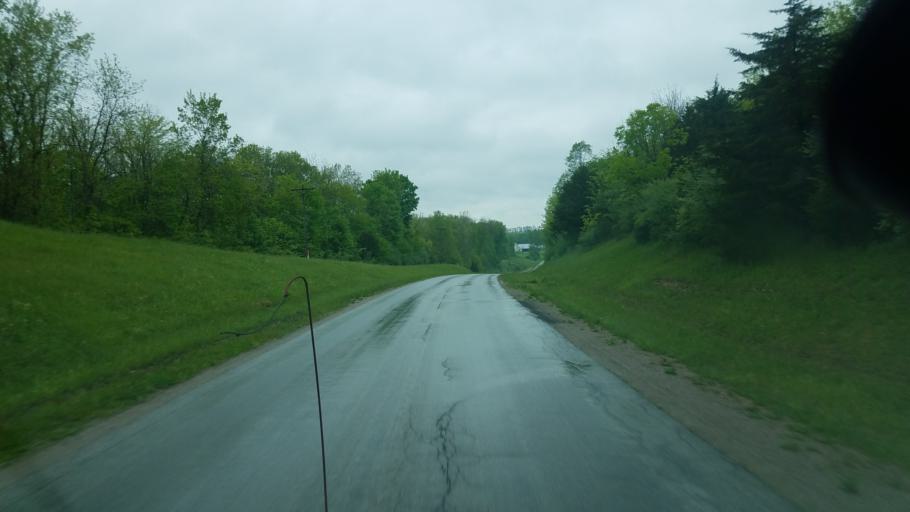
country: US
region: Ohio
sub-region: Highland County
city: Greenfield
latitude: 39.2896
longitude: -83.4605
